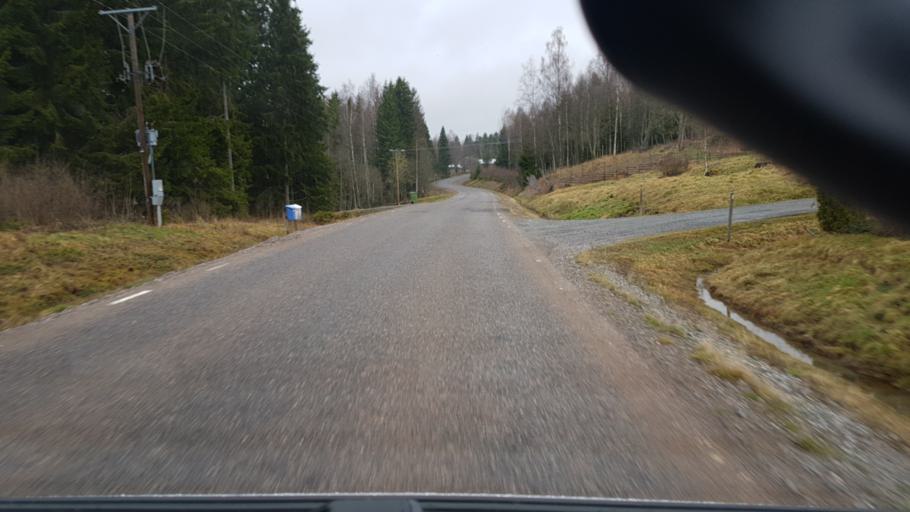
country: SE
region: Vaermland
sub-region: Eda Kommun
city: Charlottenberg
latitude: 59.9777
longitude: 12.4016
